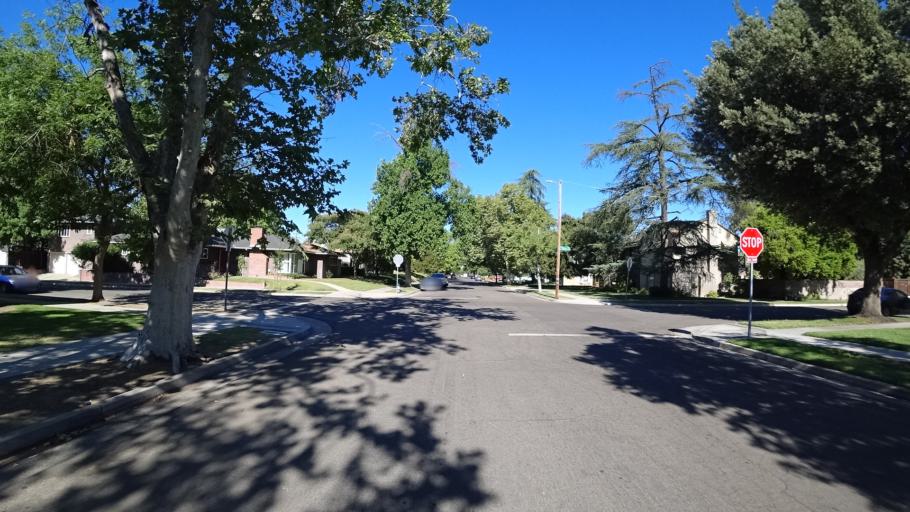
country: US
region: California
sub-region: Fresno County
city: Fresno
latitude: 36.7758
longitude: -119.8062
